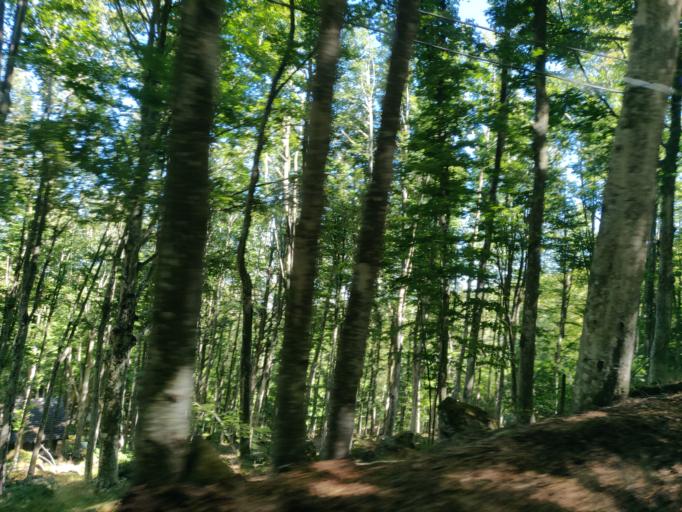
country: IT
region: Tuscany
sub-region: Provincia di Siena
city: Abbadia San Salvatore
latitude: 42.8967
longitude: 11.6284
